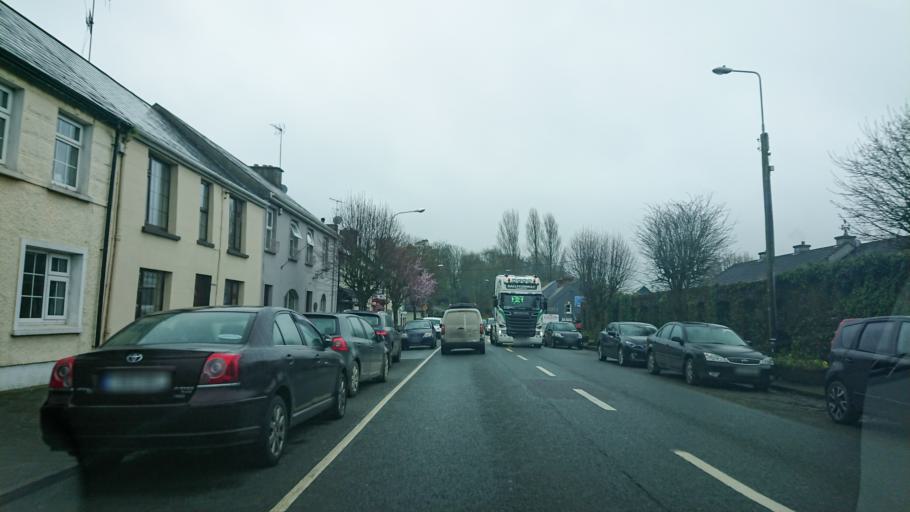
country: IE
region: Munster
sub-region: County Cork
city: Bandon
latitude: 51.7647
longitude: -8.6567
